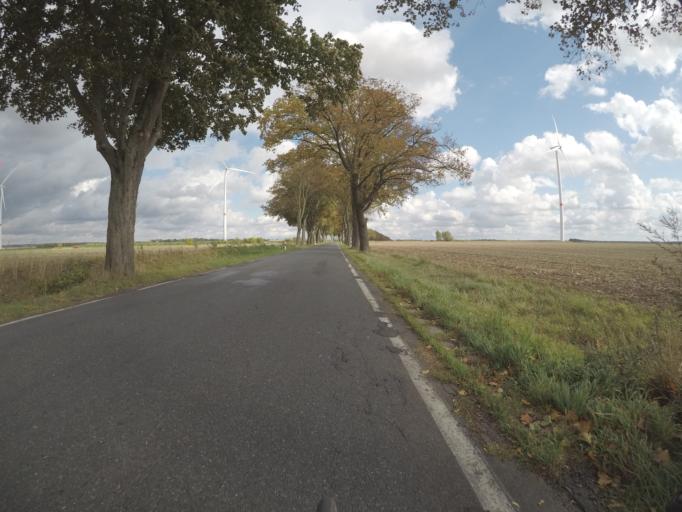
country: DE
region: Brandenburg
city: Werftpfuhl
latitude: 52.6041
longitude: 13.7854
